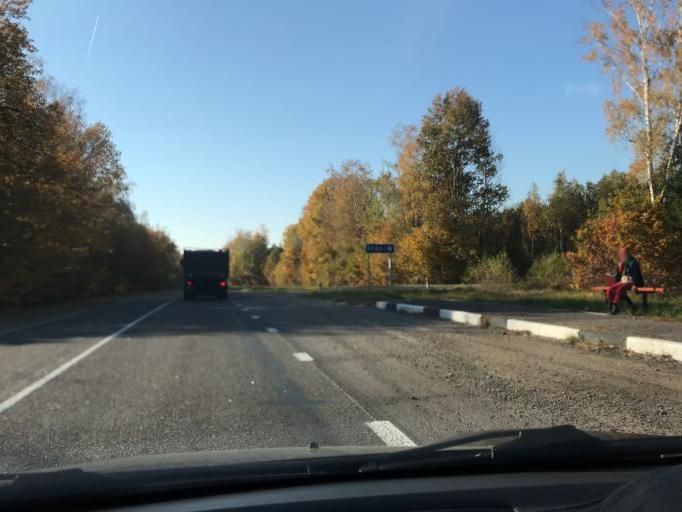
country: BY
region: Mogilev
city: Hlusha
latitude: 53.0914
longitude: 28.9161
